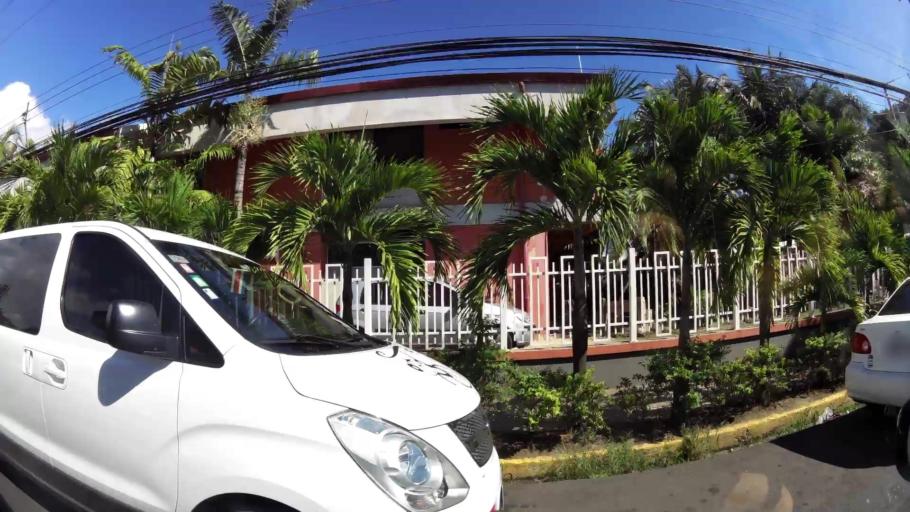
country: CR
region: Puntarenas
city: Quepos
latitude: 9.4310
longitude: -84.1639
